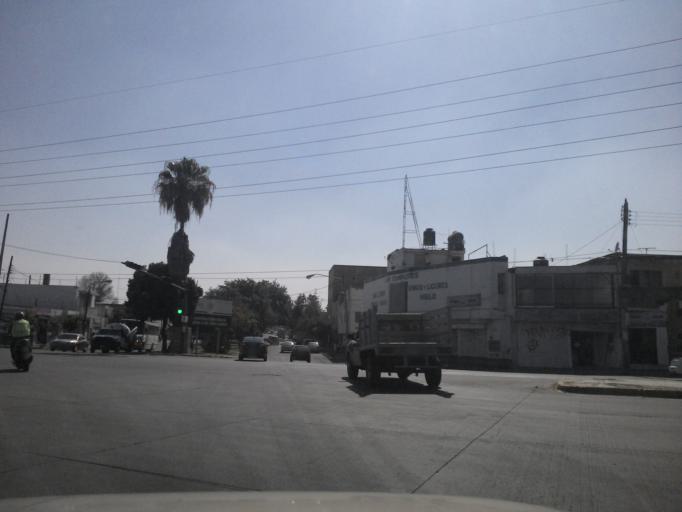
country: MX
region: Jalisco
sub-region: Zapopan
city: Zapopan
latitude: 20.7013
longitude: -103.3577
